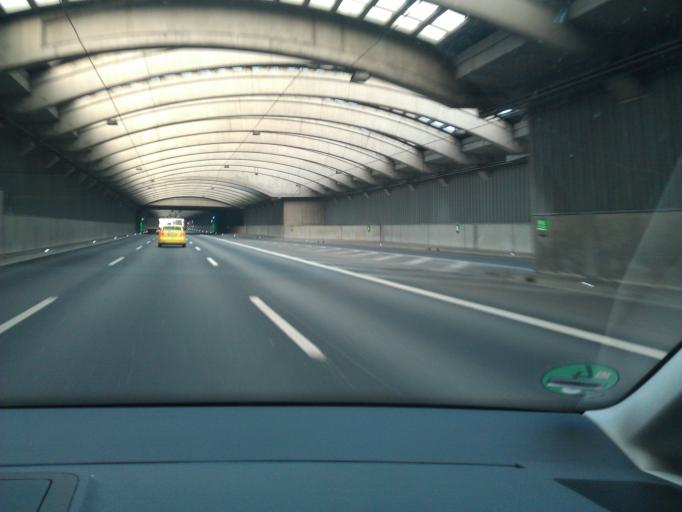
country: DE
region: North Rhine-Westphalia
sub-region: Regierungsbezirk Koln
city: Mengenich
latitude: 50.9405
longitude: 6.8496
